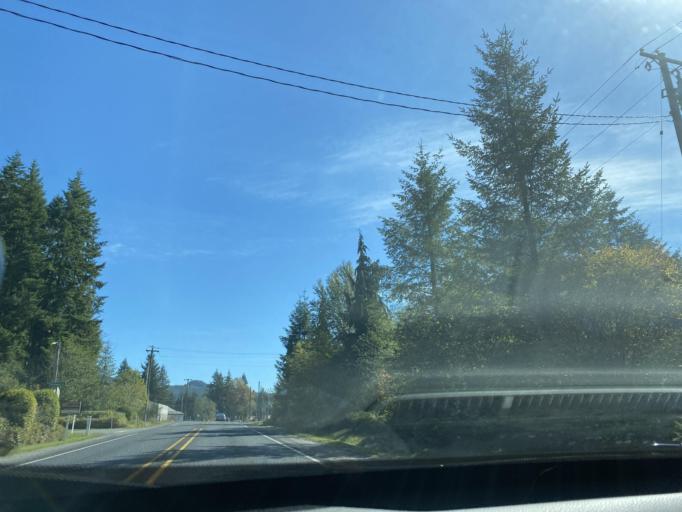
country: US
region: Washington
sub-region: Clallam County
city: Forks
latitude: 47.9582
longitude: -124.3900
